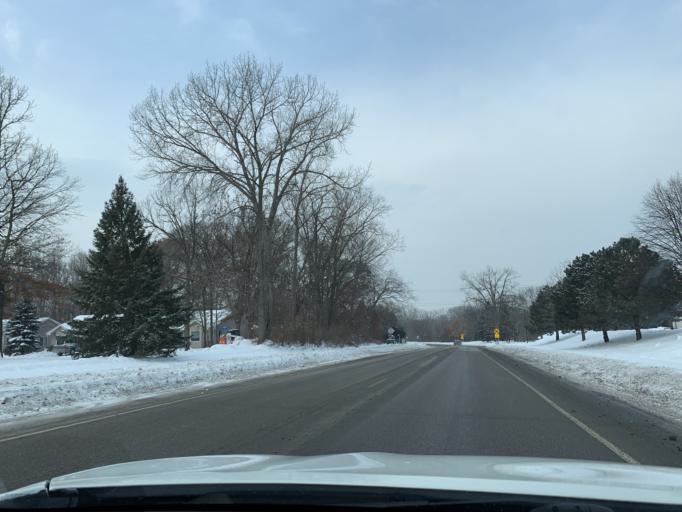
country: US
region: Minnesota
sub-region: Anoka County
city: Coon Rapids
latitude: 45.1626
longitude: -93.2905
